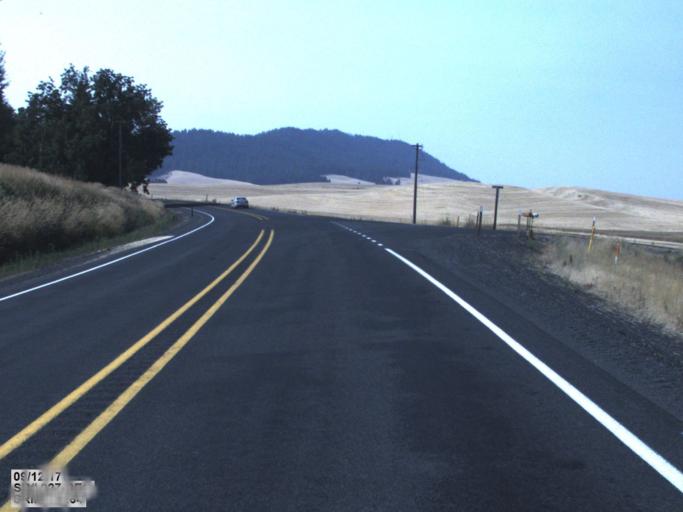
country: US
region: Washington
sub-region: Whitman County
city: Pullman
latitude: 46.8916
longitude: -117.1163
